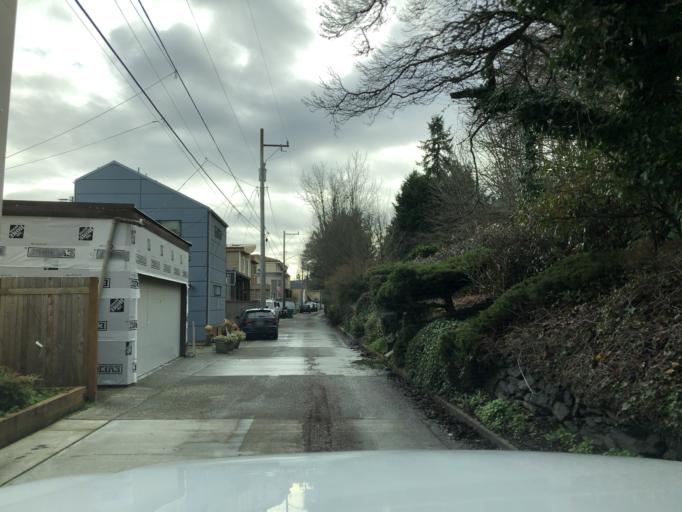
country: US
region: Washington
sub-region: King County
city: Lake Forest Park
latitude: 47.7137
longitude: -122.2773
